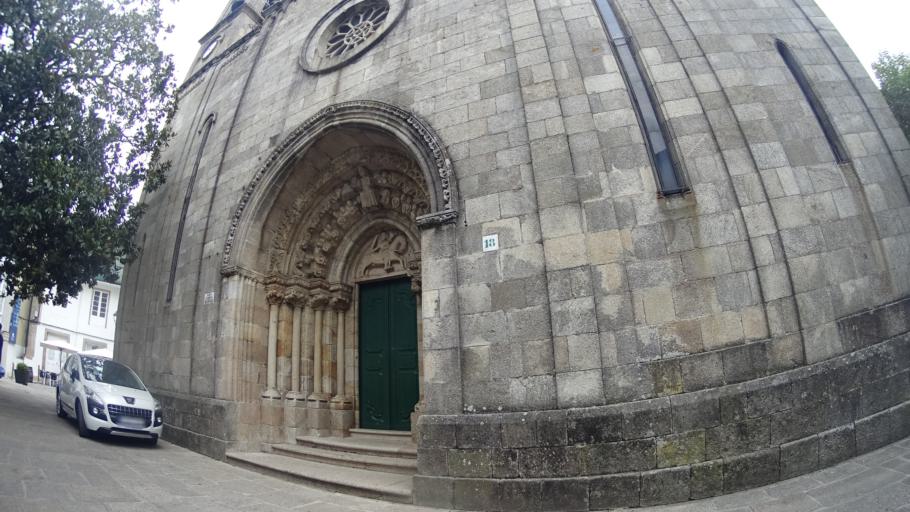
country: ES
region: Galicia
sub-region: Provincia da Coruna
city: Betanzos
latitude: 43.2808
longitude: -8.2118
